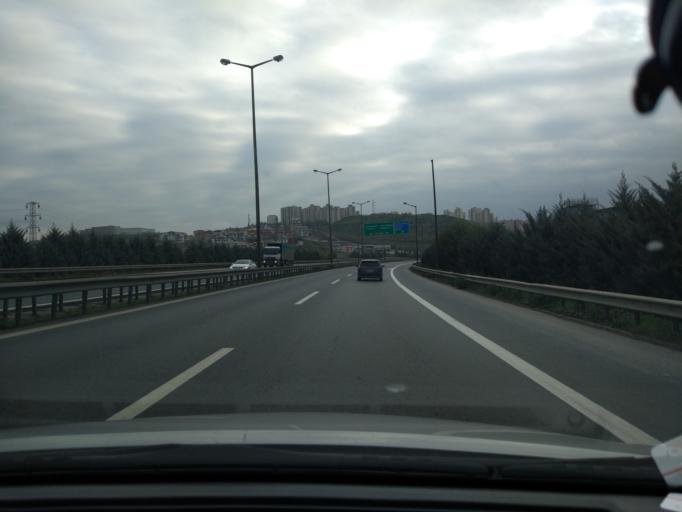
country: TR
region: Kocaeli
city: Izmit
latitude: 40.7847
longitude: 29.9722
